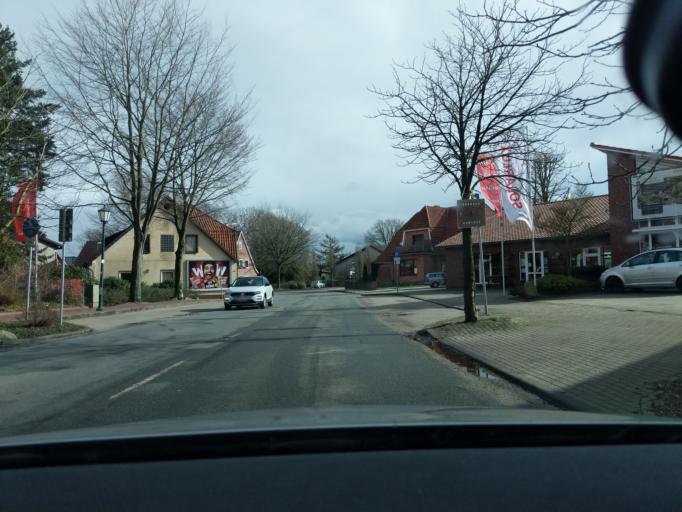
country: DE
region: Lower Saxony
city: Oldendorf
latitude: 53.5906
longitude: 9.2534
